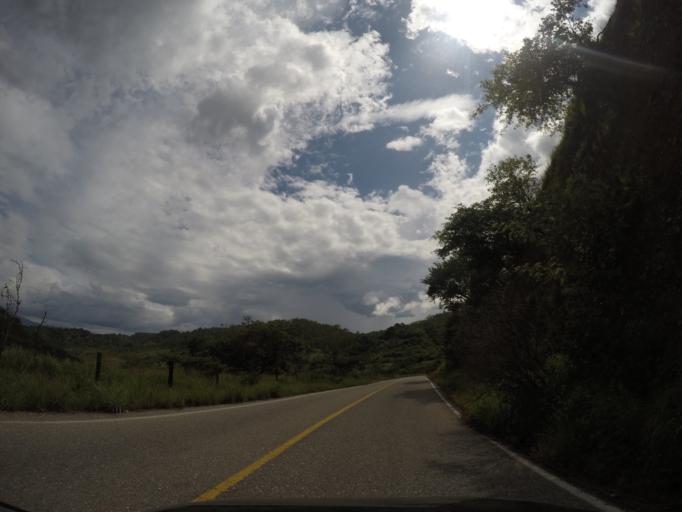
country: MX
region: Oaxaca
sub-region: San Jeronimo Coatlan
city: San Cristobal Honduras
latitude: 16.4248
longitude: -97.0704
